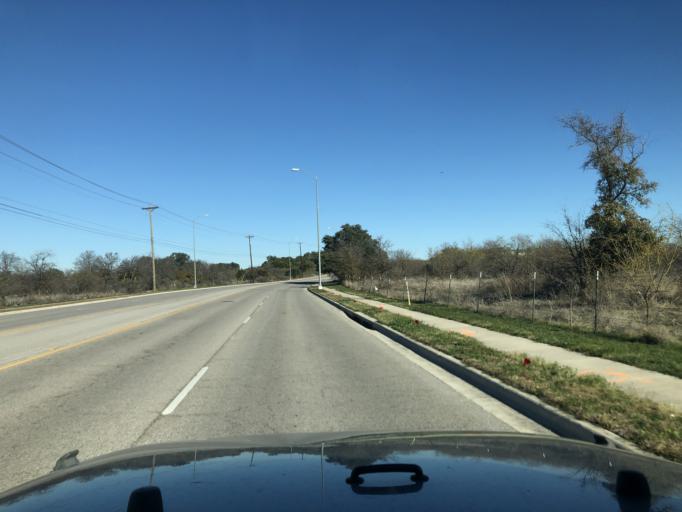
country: US
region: Texas
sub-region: Williamson County
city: Round Rock
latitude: 30.5288
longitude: -97.6948
